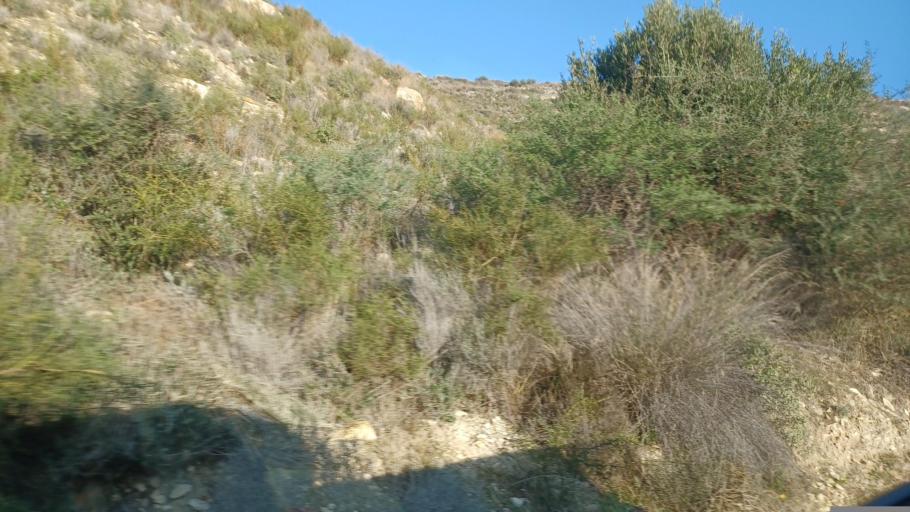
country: CY
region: Larnaka
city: Kofinou
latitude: 34.8280
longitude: 33.3090
